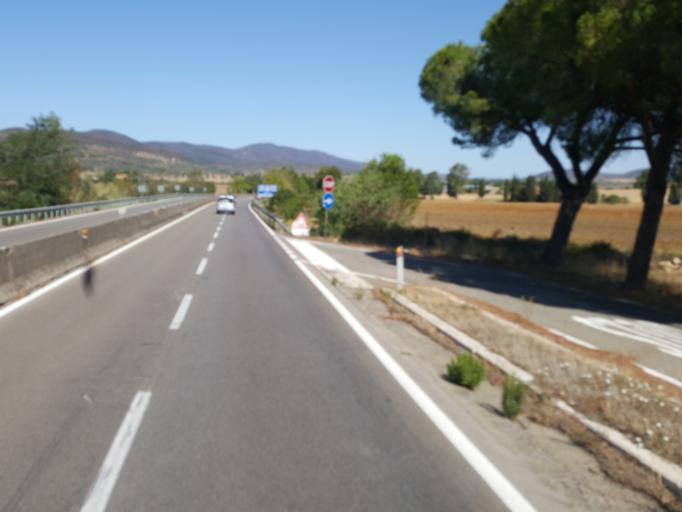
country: IT
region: Tuscany
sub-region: Provincia di Grosseto
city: Fonteblanda
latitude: 42.5686
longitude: 11.1704
